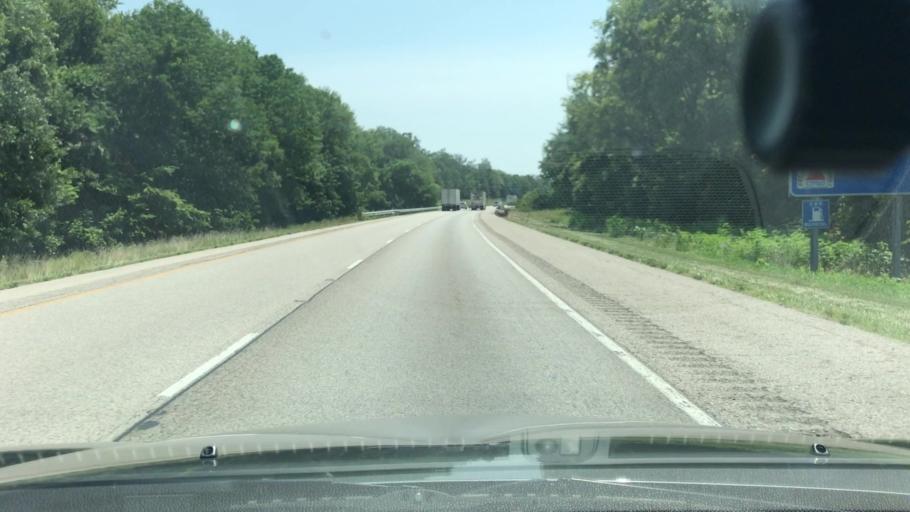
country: US
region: Illinois
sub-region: Washington County
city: Nashville
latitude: 38.3994
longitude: -89.3961
